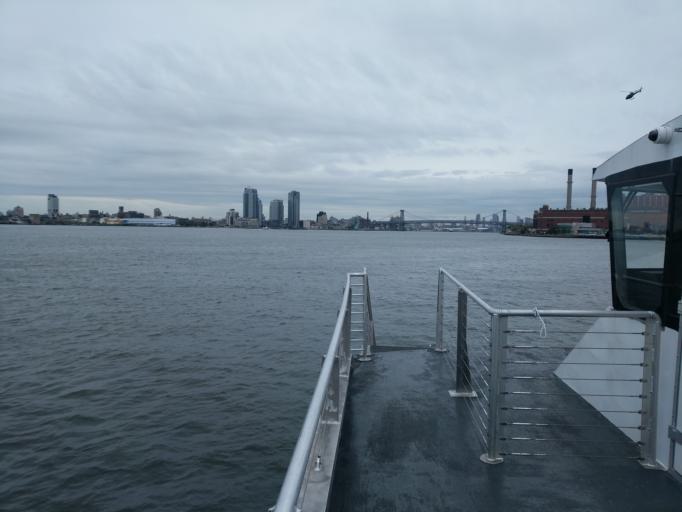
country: US
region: New York
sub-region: Queens County
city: Long Island City
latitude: 40.7356
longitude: -73.9692
